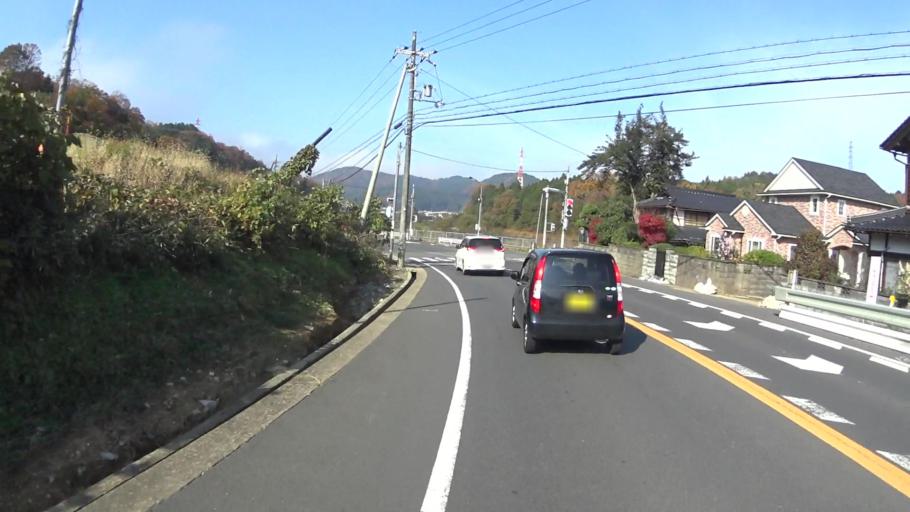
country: JP
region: Kyoto
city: Fukuchiyama
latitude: 35.2719
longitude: 135.1470
